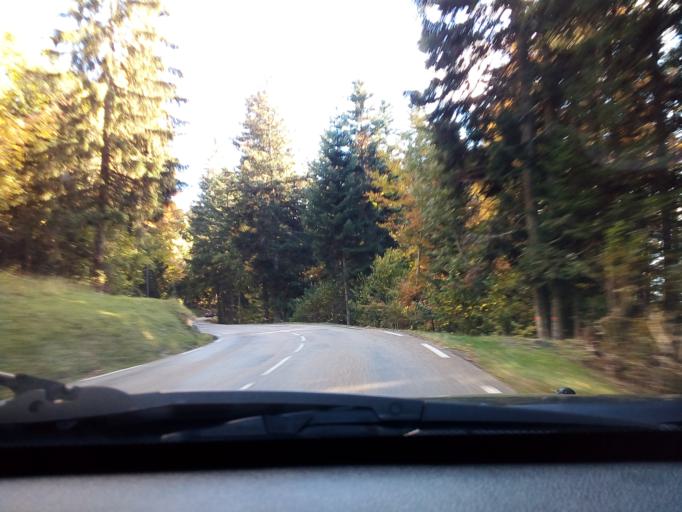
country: FR
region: Rhone-Alpes
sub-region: Departement de l'Isere
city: Le Sappey-en-Chartreuse
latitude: 45.2788
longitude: 5.7660
